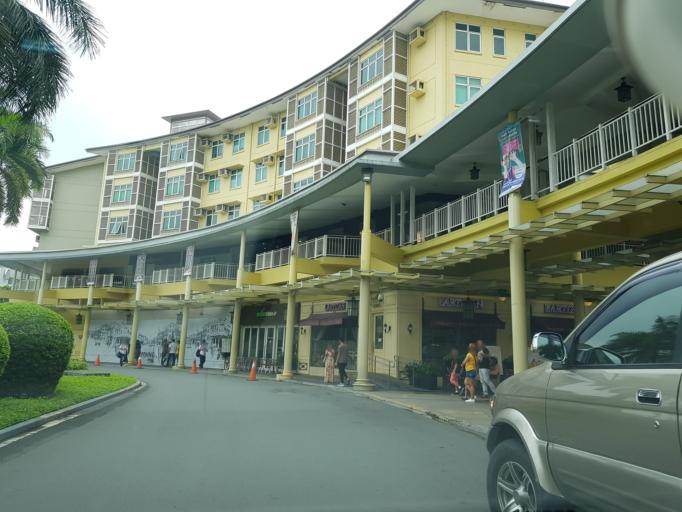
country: PH
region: Calabarzon
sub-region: Province of Rizal
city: Pateros
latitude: 14.5497
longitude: 121.0546
